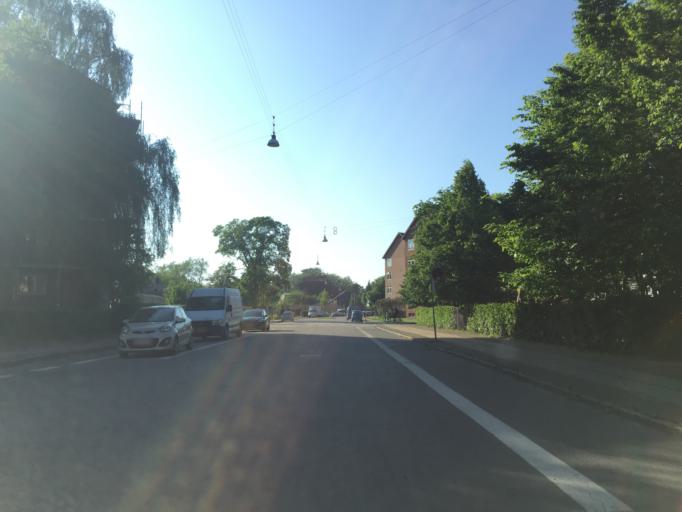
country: DK
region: Capital Region
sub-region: Frederiksberg Kommune
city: Frederiksberg
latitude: 55.6567
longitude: 12.5357
